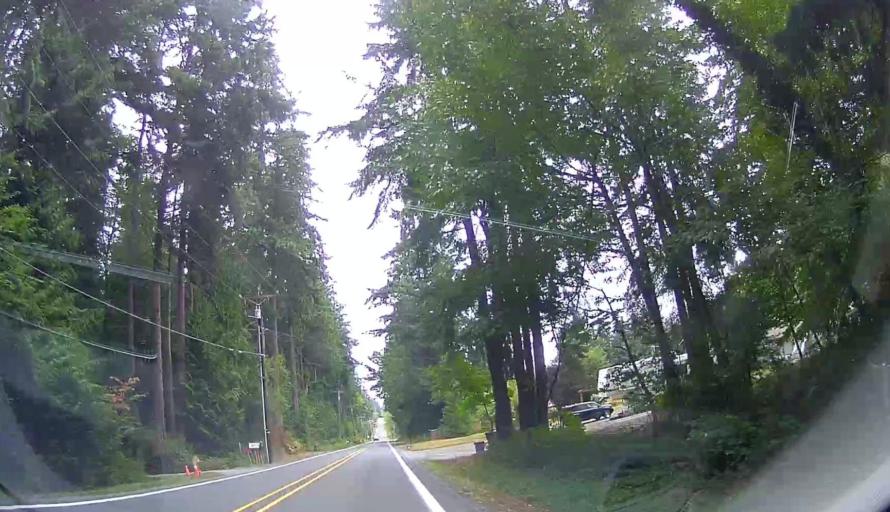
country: US
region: Washington
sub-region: Snohomish County
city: Warm Beach
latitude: 48.1538
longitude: -122.3612
